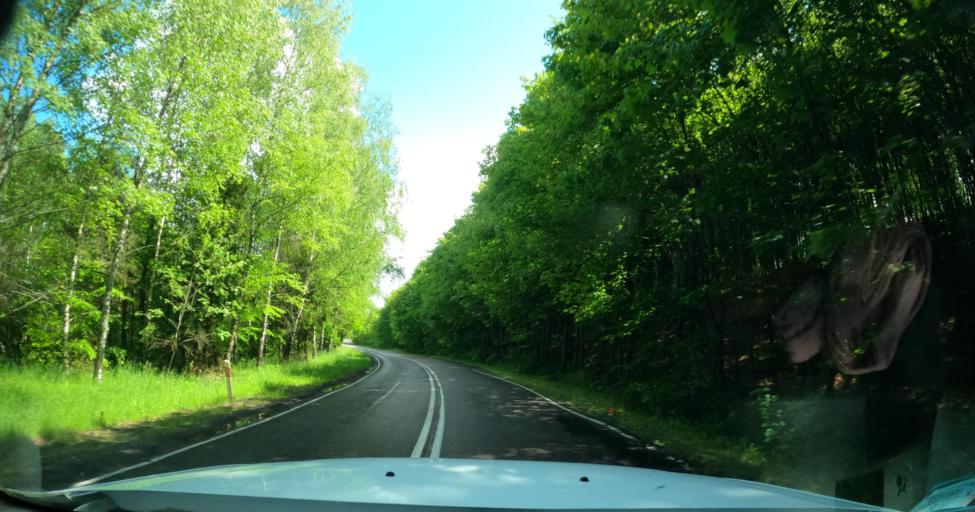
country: PL
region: Pomeranian Voivodeship
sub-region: Powiat bytowski
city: Czarna Dabrowka
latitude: 54.3760
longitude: 17.4957
